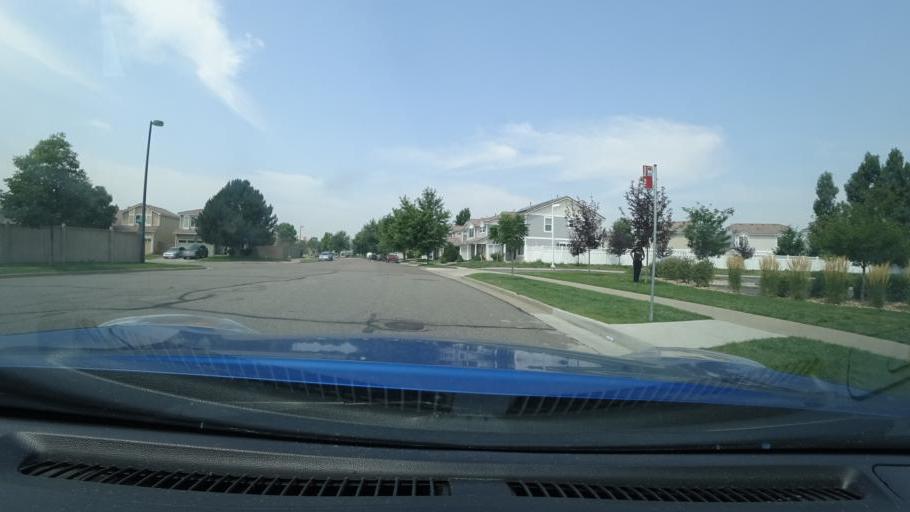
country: US
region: Colorado
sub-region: Adams County
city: Aurora
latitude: 39.7819
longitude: -104.7568
